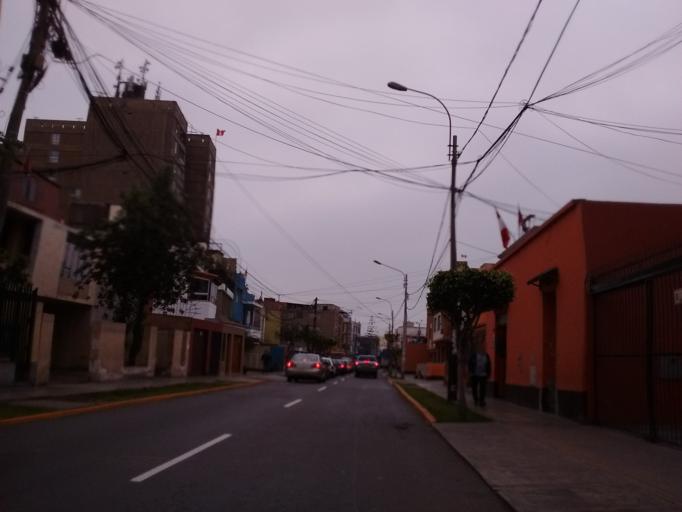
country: PE
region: Lima
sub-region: Lima
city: San Isidro
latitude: -12.0776
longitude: -77.0635
